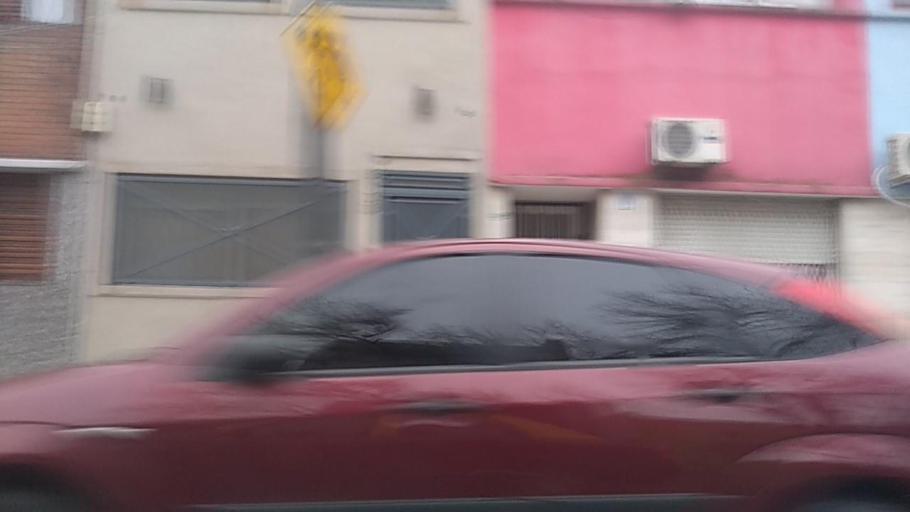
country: AR
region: Buenos Aires F.D.
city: Villa Santa Rita
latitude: -34.5989
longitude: -58.4957
